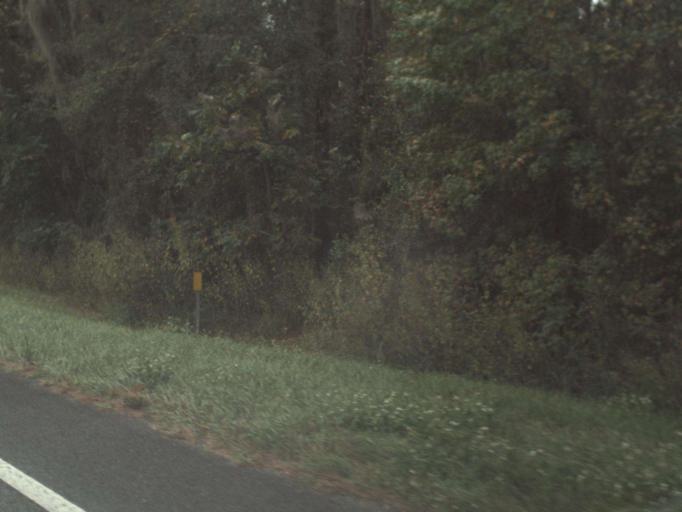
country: US
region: Florida
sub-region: Jefferson County
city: Monticello
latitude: 30.6558
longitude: -83.8773
